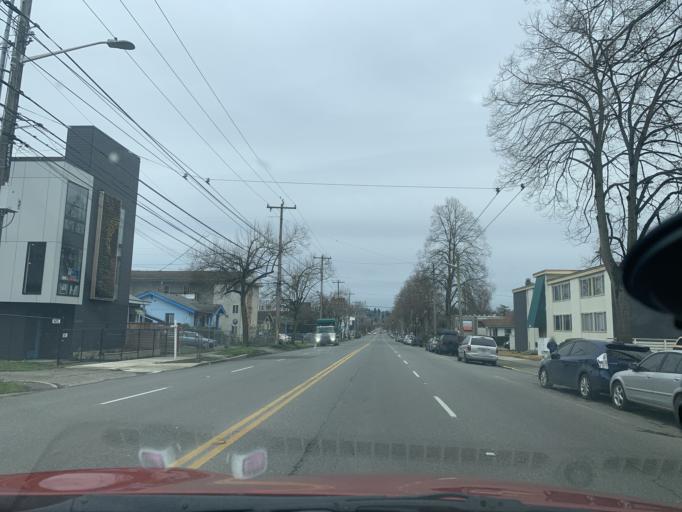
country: US
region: Washington
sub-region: King County
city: Bryn Mawr-Skyway
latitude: 47.5354
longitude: -122.2700
